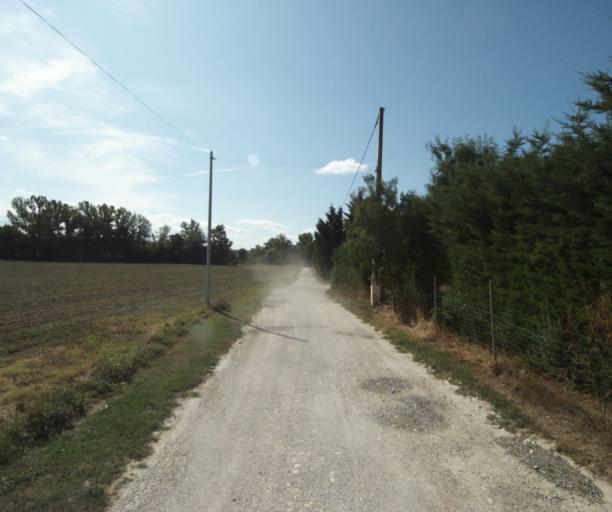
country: FR
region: Midi-Pyrenees
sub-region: Departement de la Haute-Garonne
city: Revel
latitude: 43.5058
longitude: 1.9675
